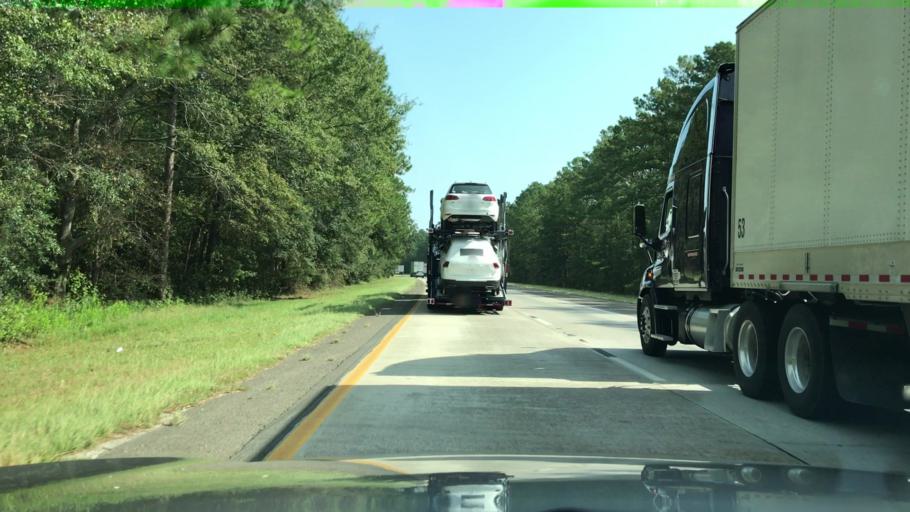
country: US
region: South Carolina
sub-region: Colleton County
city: Walterboro
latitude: 32.8225
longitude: -80.7523
